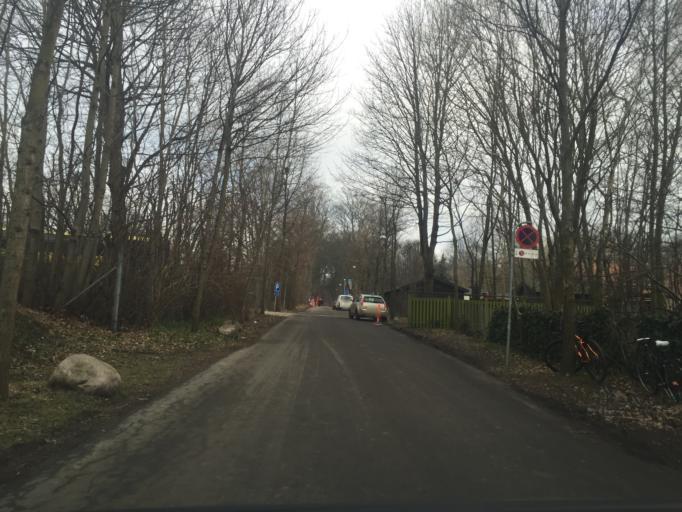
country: DK
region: Capital Region
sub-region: Gentofte Kommune
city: Charlottenlund
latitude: 55.7227
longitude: 12.5643
